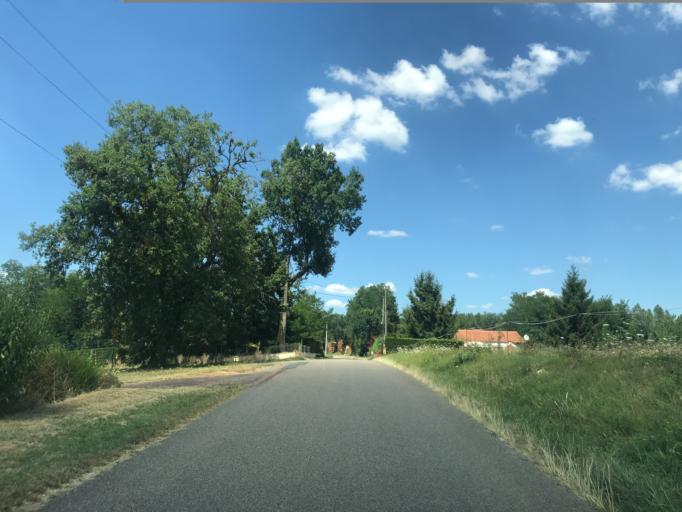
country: FR
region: Aquitaine
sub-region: Departement de la Dordogne
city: Sarlat-la-Caneda
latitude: 44.8553
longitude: 1.2054
